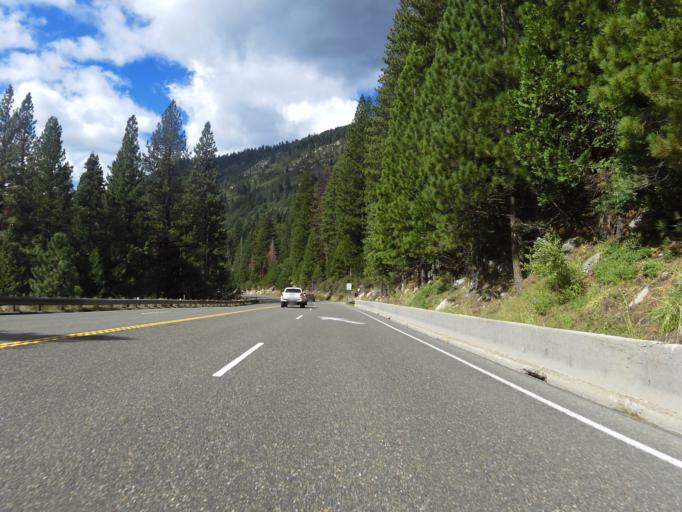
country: US
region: California
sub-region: El Dorado County
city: South Lake Tahoe
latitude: 38.8091
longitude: -120.1332
